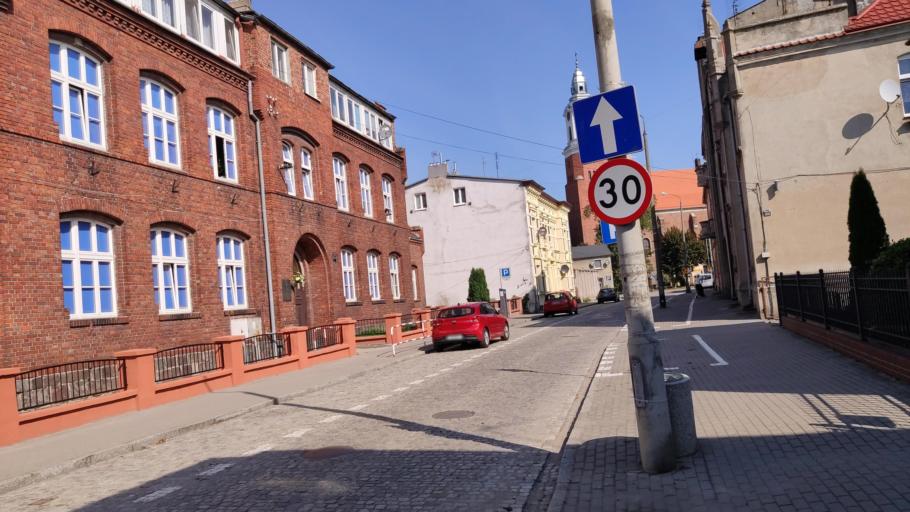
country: PL
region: Kujawsko-Pomorskie
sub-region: Powiat zninski
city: Znin
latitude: 52.8457
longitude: 17.7273
